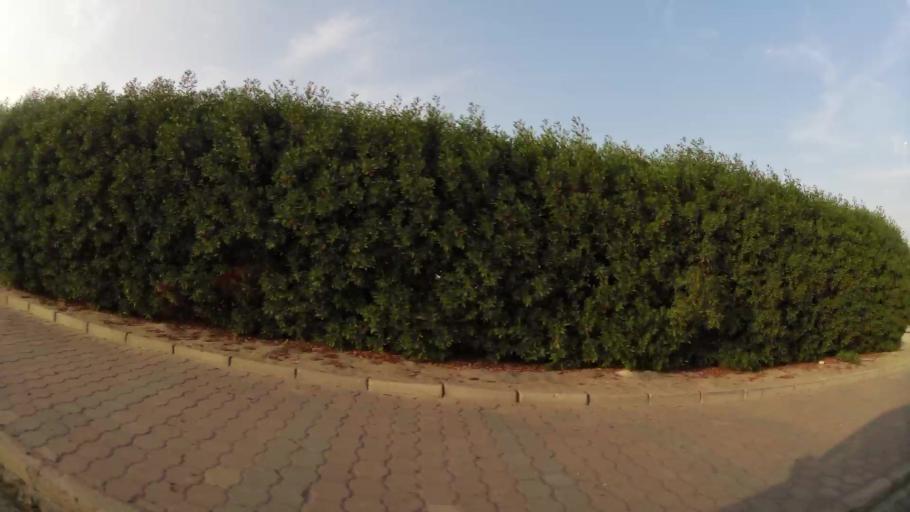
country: KW
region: Mubarak al Kabir
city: Sabah as Salim
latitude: 29.2495
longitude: 48.0754
